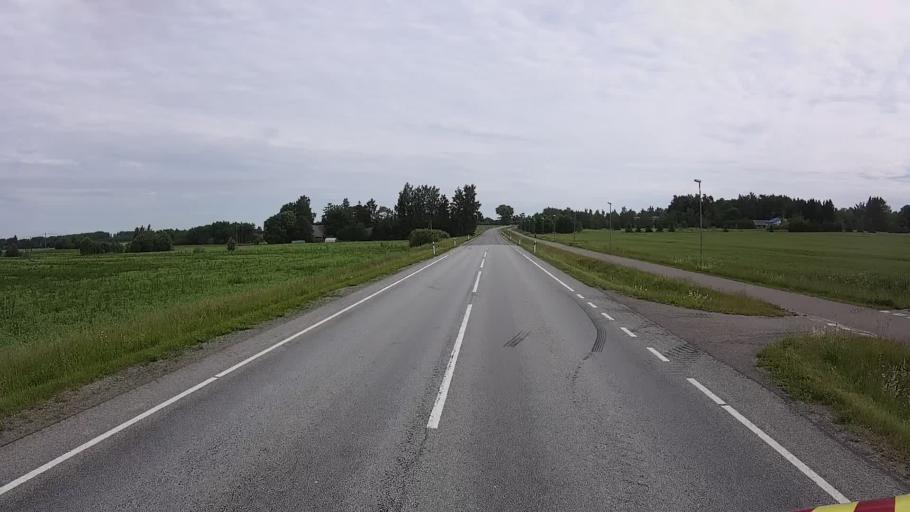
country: EE
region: Viljandimaa
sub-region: Karksi vald
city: Karksi-Nuia
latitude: 58.1122
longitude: 25.5709
